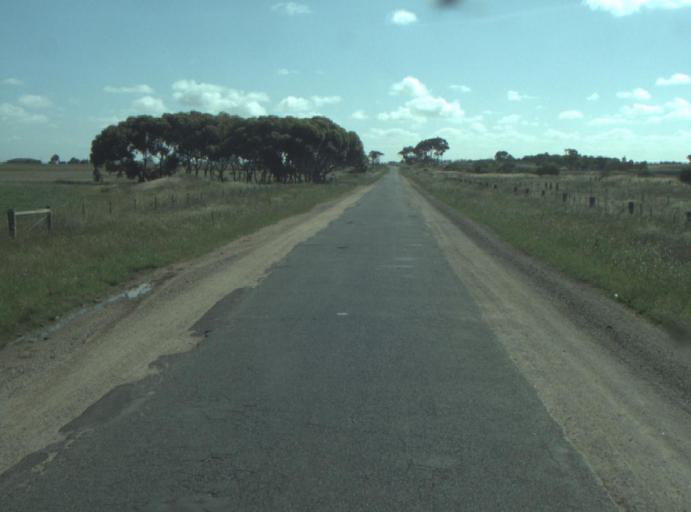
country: AU
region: Victoria
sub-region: Wyndham
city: Little River
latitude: -37.9928
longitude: 144.4522
